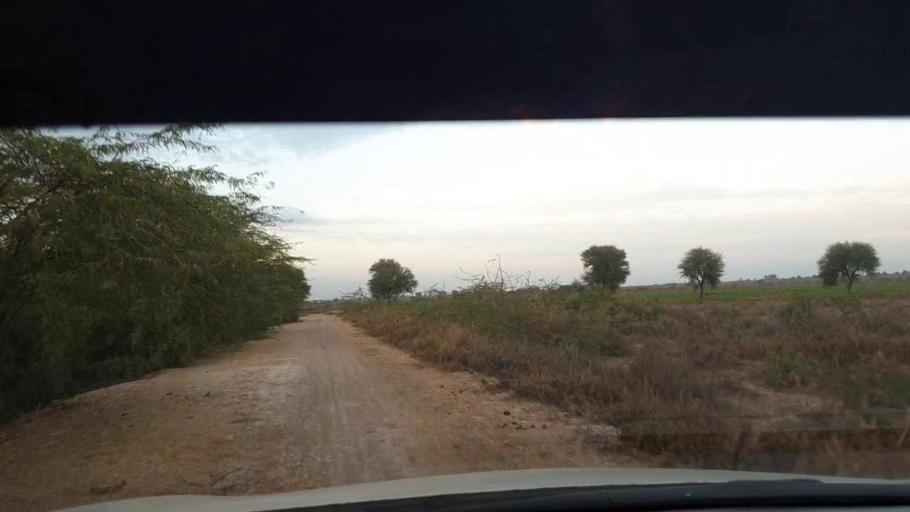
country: PK
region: Sindh
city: Berani
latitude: 25.8029
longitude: 68.8088
